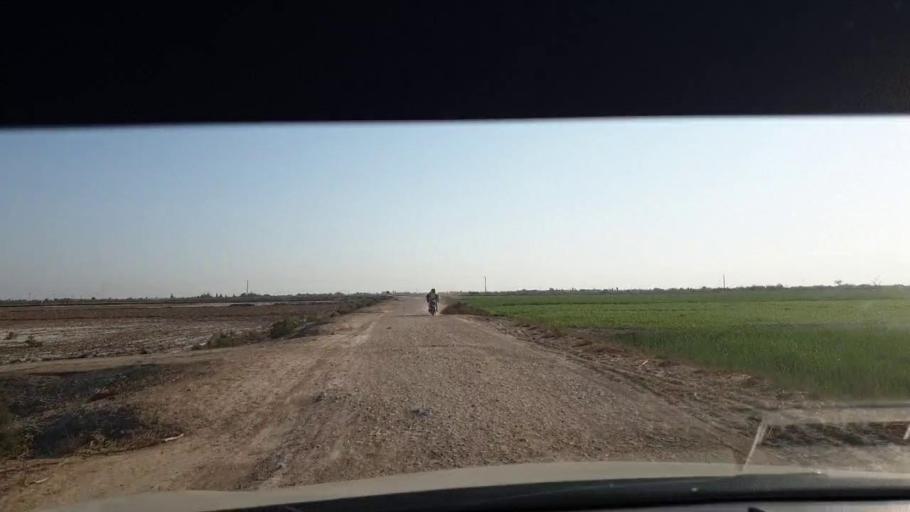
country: PK
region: Sindh
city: Berani
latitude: 25.7924
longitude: 68.9264
